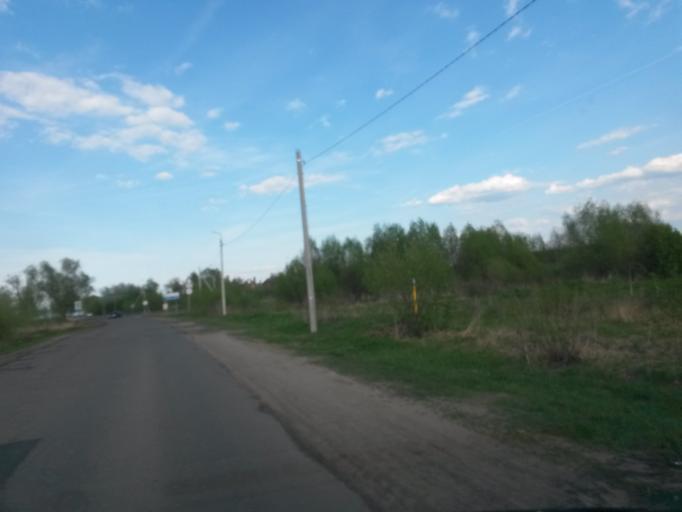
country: RU
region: Jaroslavl
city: Myshkin
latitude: 57.7811
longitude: 38.4492
